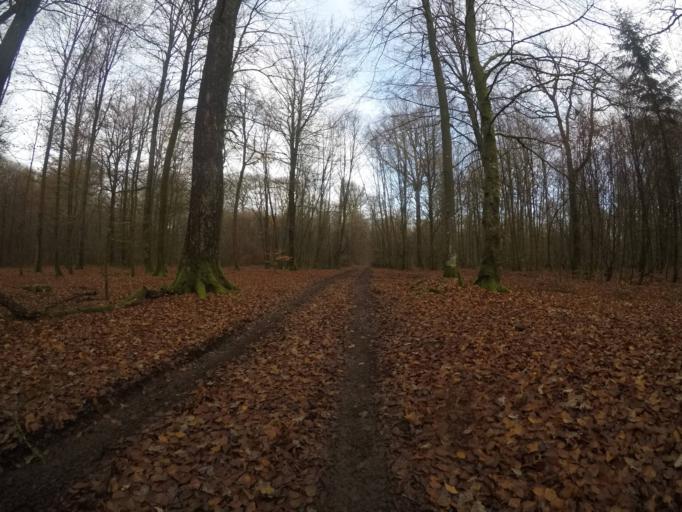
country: BE
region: Wallonia
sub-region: Province du Luxembourg
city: Habay-la-Vieille
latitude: 49.7423
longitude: 5.5934
